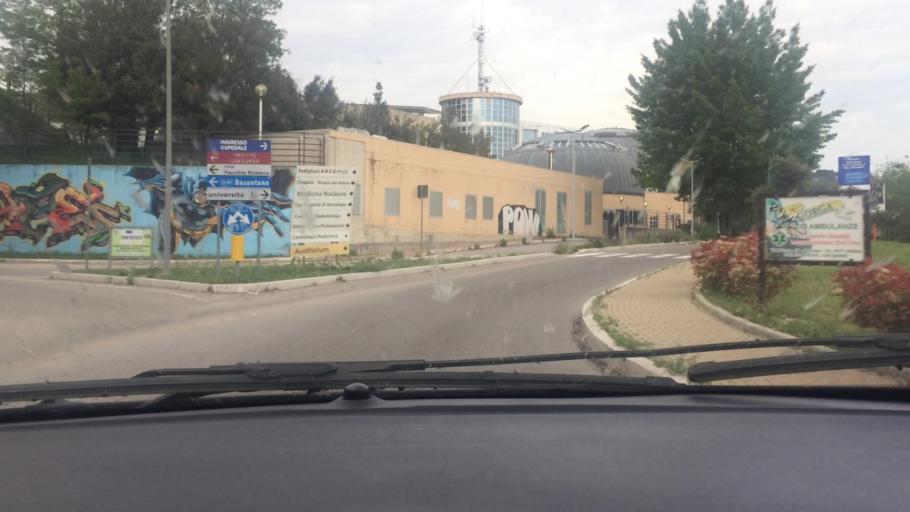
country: IT
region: Basilicate
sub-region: Provincia di Potenza
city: Potenza
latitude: 40.6524
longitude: 15.8019
